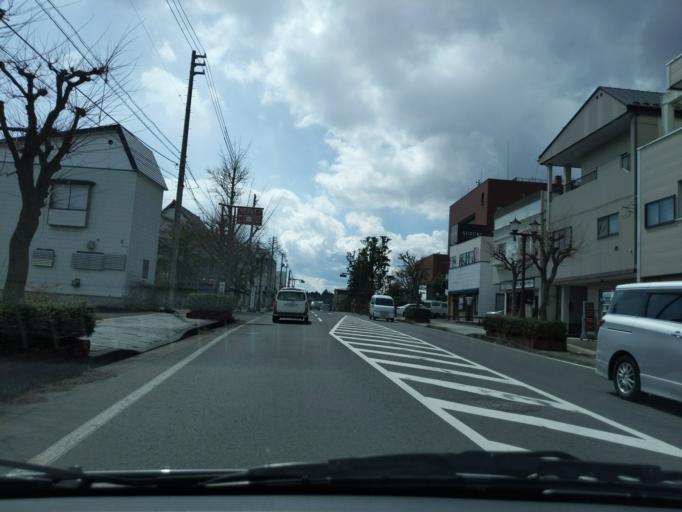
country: JP
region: Iwate
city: Mizusawa
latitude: 39.1455
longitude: 141.1401
